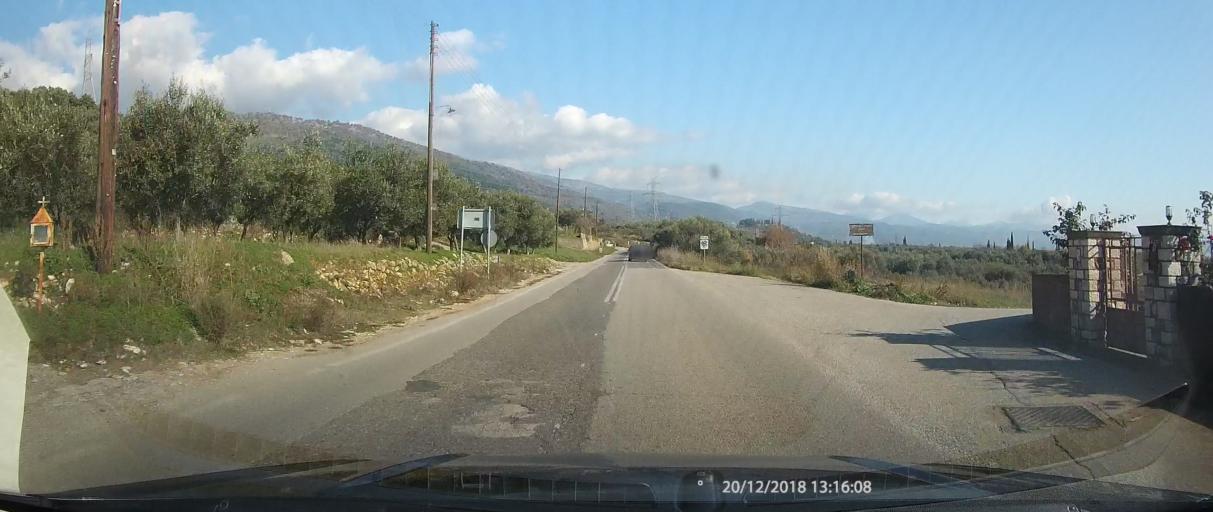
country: GR
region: West Greece
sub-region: Nomos Aitolias kai Akarnanias
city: Paravola
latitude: 38.6101
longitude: 21.5055
